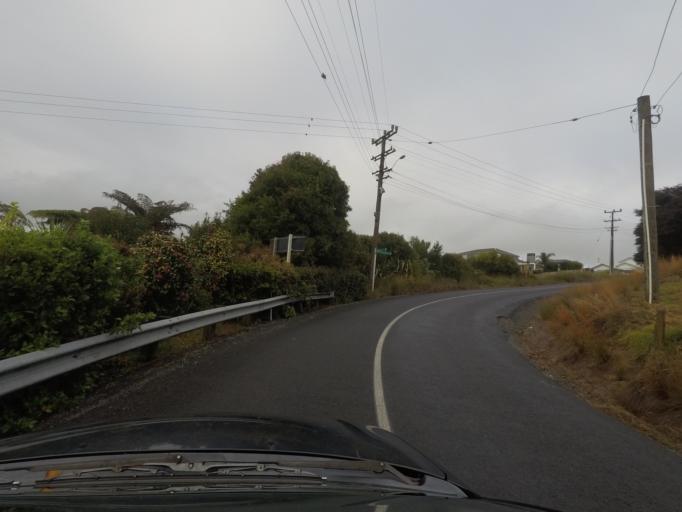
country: NZ
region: Auckland
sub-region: Auckland
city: Rosebank
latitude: -36.7625
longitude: 174.5975
